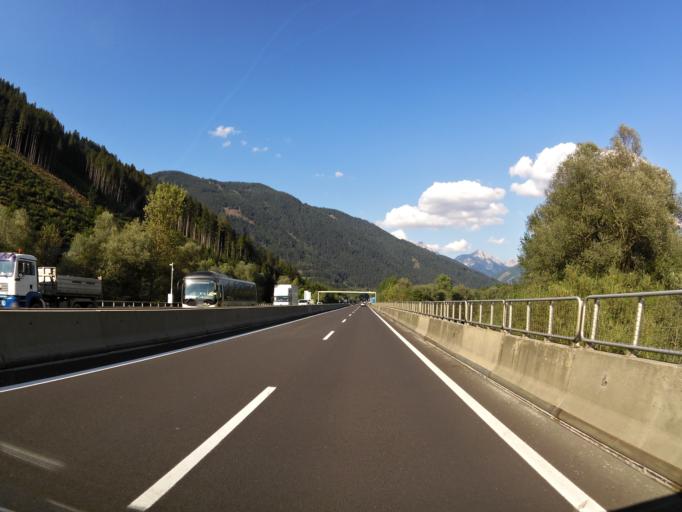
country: AT
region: Styria
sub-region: Politischer Bezirk Liezen
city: Selzthal
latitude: 47.5642
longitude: 14.3070
